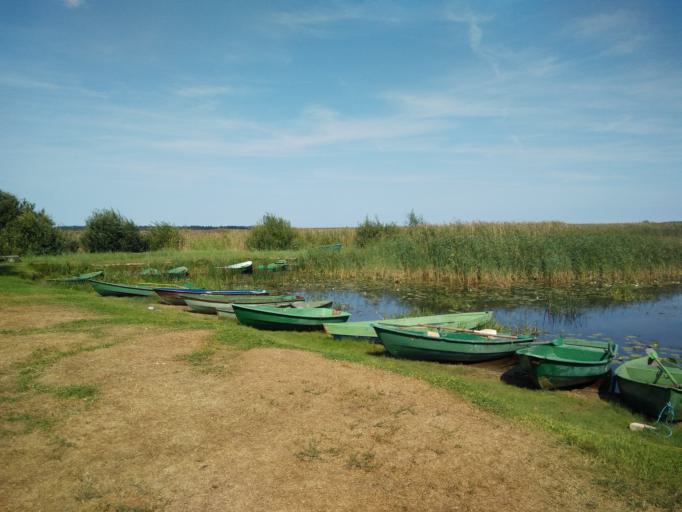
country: LV
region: Mesraga
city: Mersrags
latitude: 57.2709
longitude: 23.0755
